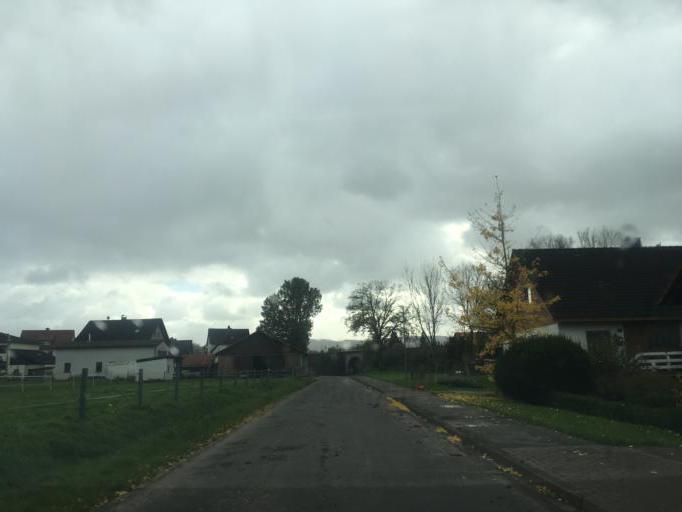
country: DE
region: Lower Saxony
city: Bodenfelde
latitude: 51.6431
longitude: 9.5597
